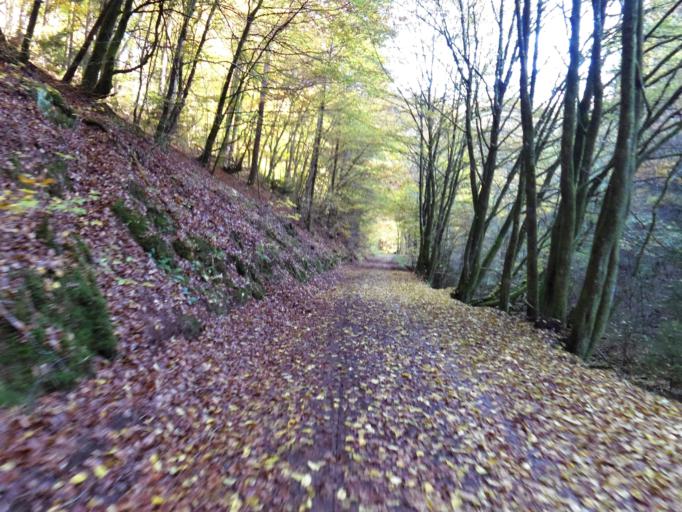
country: DE
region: Rheinland-Pfalz
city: Frankenstein
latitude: 49.4522
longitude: 7.9594
